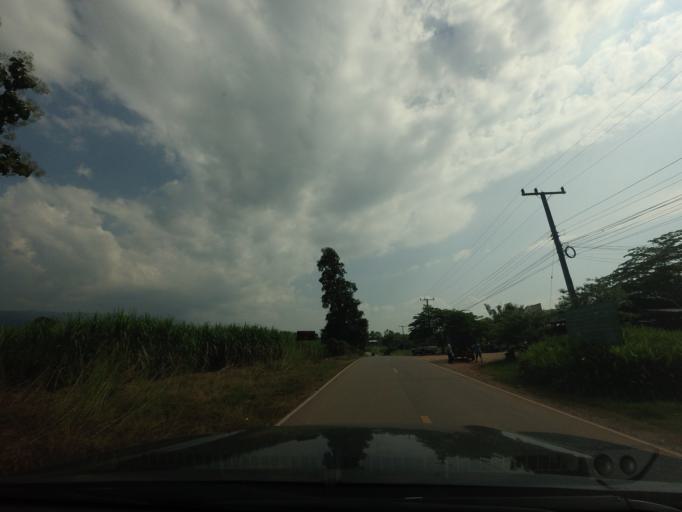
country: TH
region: Phitsanulok
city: Nakhon Thai
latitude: 17.0470
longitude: 100.9100
